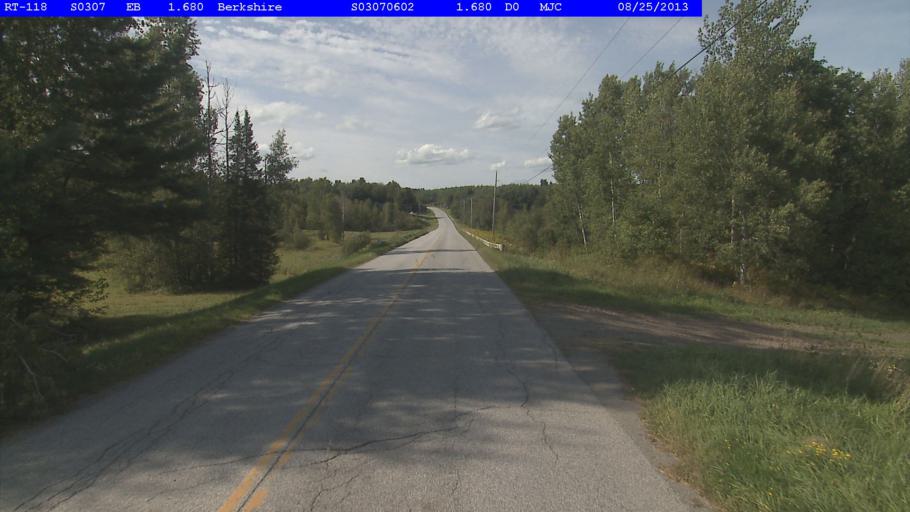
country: US
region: Vermont
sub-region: Franklin County
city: Enosburg Falls
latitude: 44.9439
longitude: -72.7404
